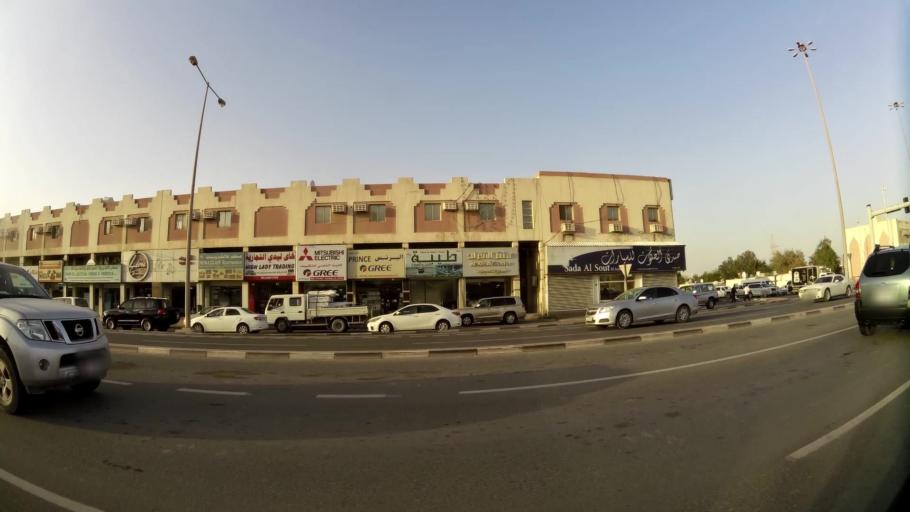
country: QA
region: Baladiyat ar Rayyan
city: Ar Rayyan
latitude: 25.3272
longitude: 51.4606
